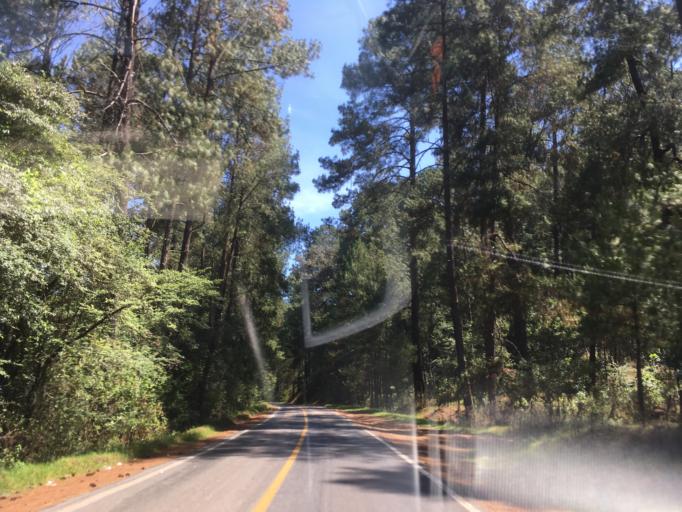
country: MX
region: Michoacan
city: Tzitzio
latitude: 19.6238
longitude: -100.7738
